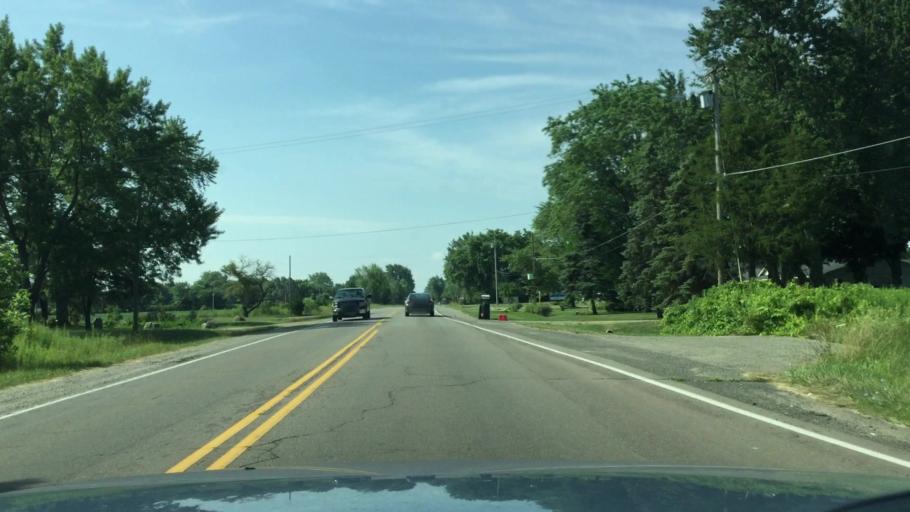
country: US
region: Michigan
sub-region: Genesee County
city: Flushing
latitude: 43.1172
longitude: -83.8138
